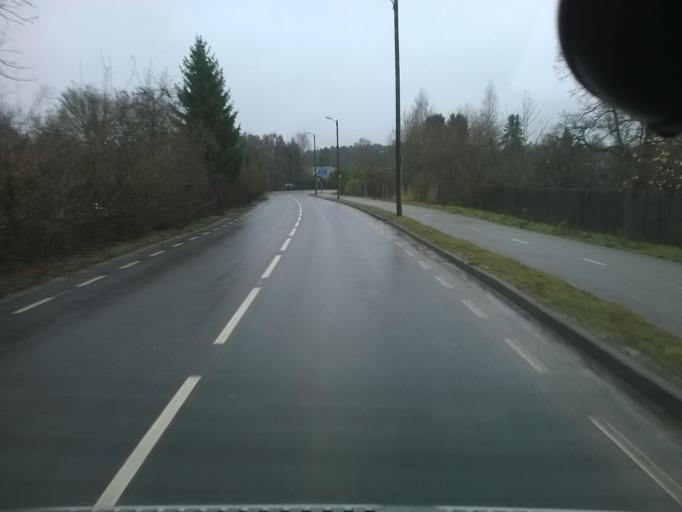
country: EE
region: Harju
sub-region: Saku vald
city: Saku
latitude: 59.2169
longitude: 24.6646
